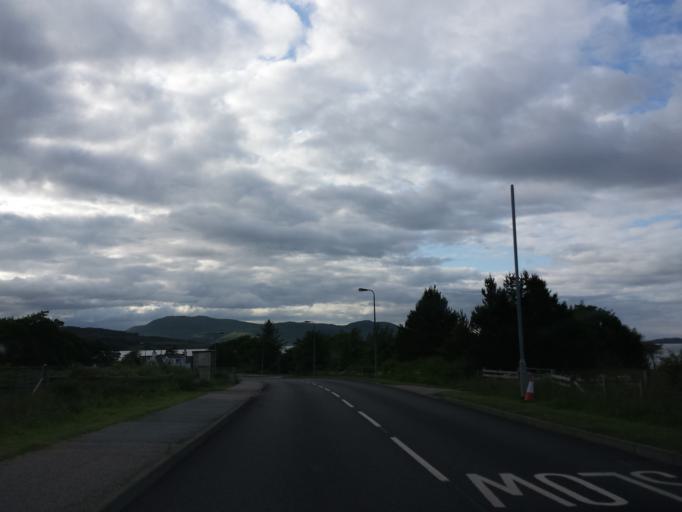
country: GB
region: Scotland
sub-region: Highland
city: Portree
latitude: 57.2374
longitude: -5.8803
